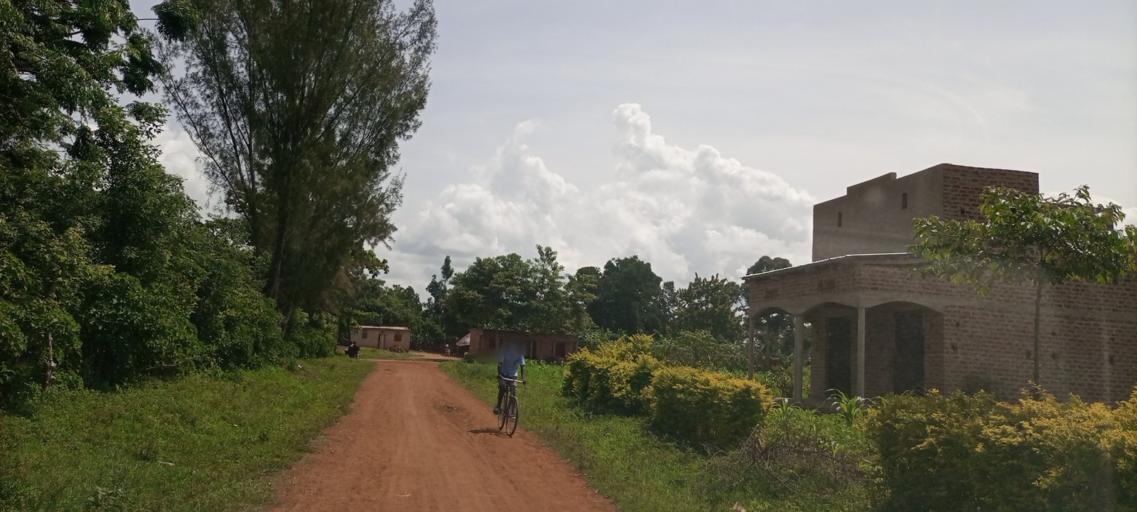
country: UG
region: Eastern Region
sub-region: Budaka District
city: Budaka
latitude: 1.1722
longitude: 33.9354
